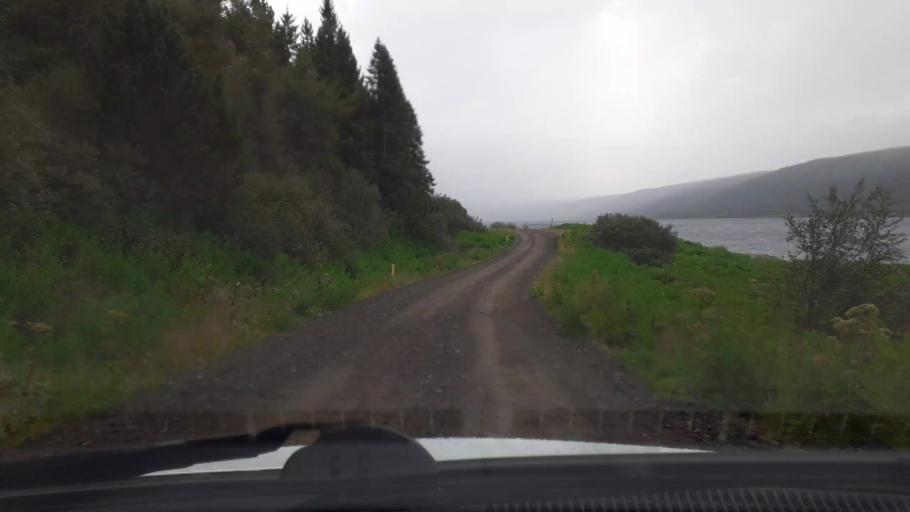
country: IS
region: Capital Region
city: Mosfellsbaer
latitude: 64.5147
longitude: -21.4112
